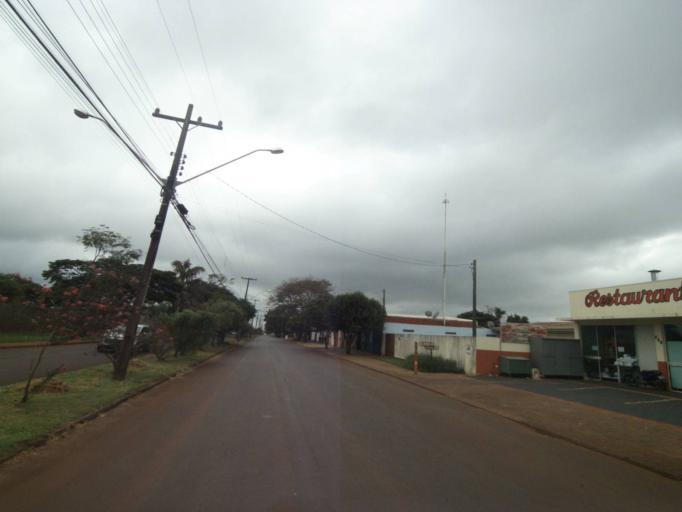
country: BR
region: Parana
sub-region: Campo Mourao
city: Campo Mourao
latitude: -24.0183
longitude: -52.3556
